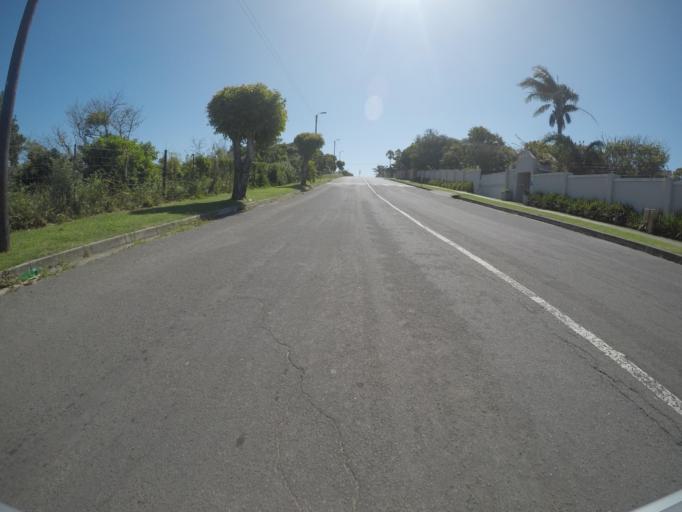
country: ZA
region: Eastern Cape
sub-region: Buffalo City Metropolitan Municipality
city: East London
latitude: -32.9887
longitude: 27.9429
